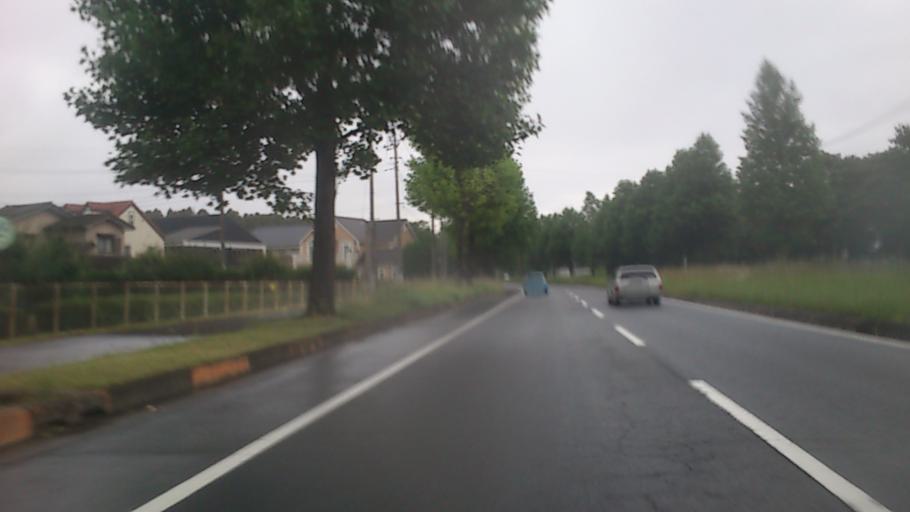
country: JP
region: Ibaraki
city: Naka
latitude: 36.0300
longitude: 140.1410
